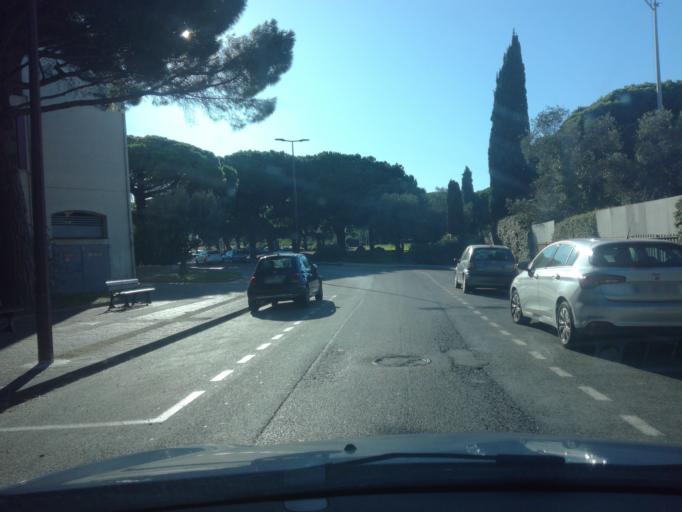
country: FR
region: Provence-Alpes-Cote d'Azur
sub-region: Departement du Var
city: Frejus
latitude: 43.4341
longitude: 6.7292
